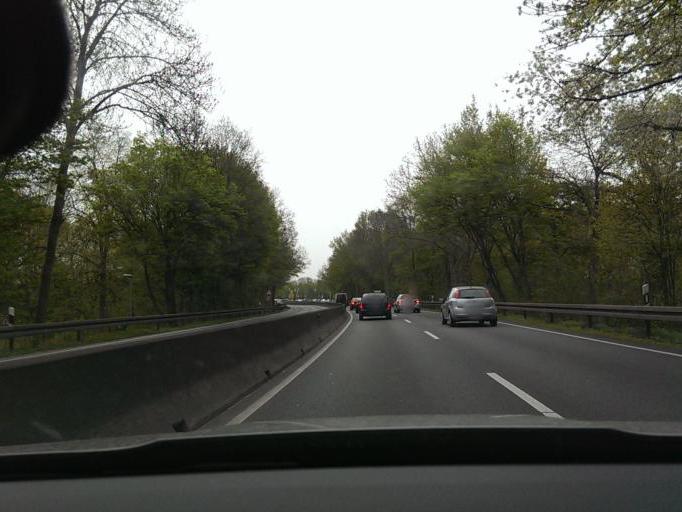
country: DE
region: Lower Saxony
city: Hannover
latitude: 52.3822
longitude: 9.6925
